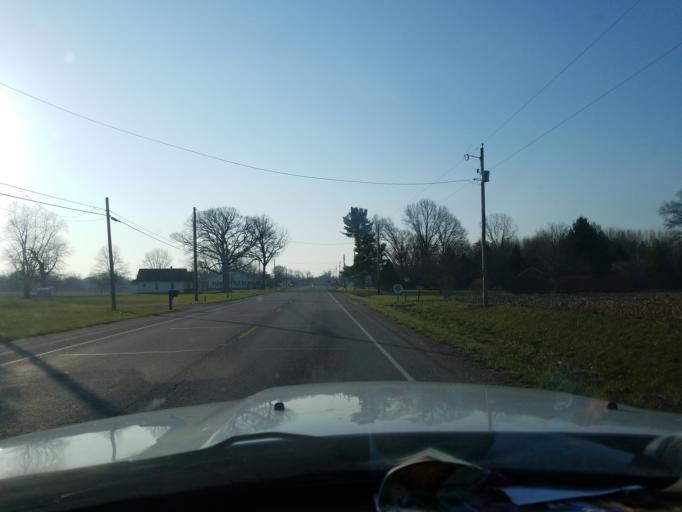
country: US
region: Indiana
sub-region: Vigo County
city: Seelyville
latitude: 39.3945
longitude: -87.3099
